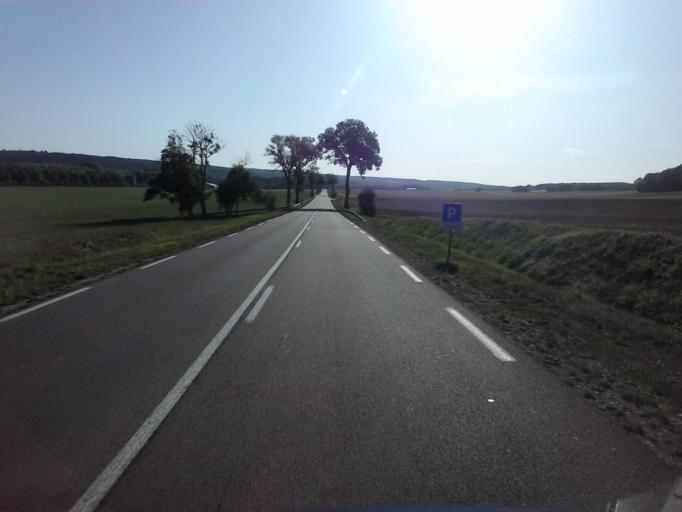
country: FR
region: Champagne-Ardenne
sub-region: Departement de l'Aube
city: Bar-sur-Seine
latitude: 48.1291
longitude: 4.3426
